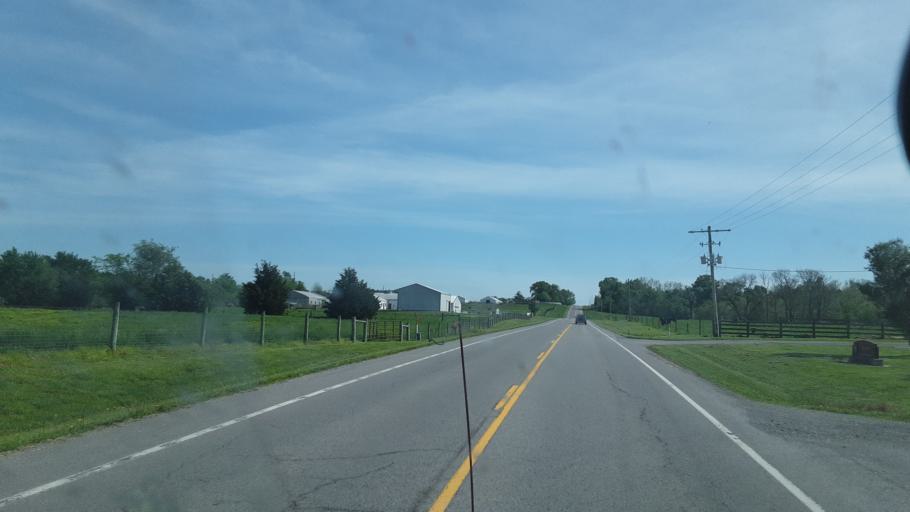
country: US
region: Illinois
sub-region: Jackson County
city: Carbondale
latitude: 37.6984
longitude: -89.2472
